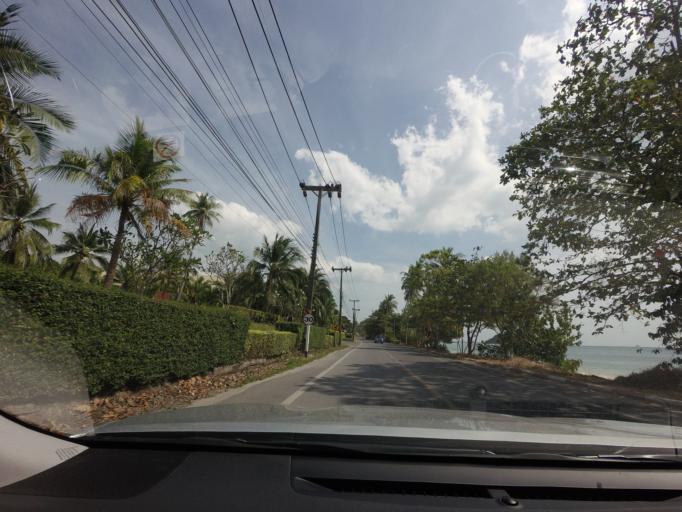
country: TH
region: Phangnga
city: Ban Ao Nang
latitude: 8.0639
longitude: 98.7452
